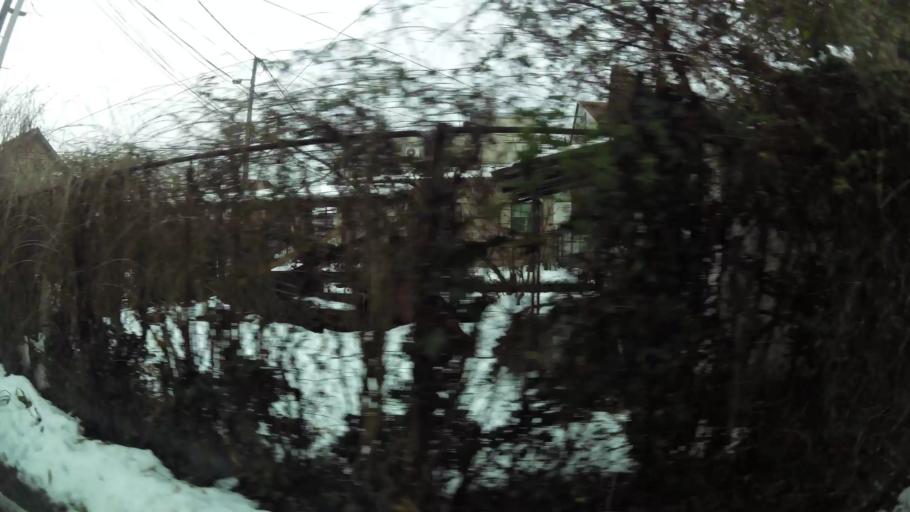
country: RS
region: Central Serbia
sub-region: Belgrade
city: Zemun
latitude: 44.8545
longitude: 20.3949
